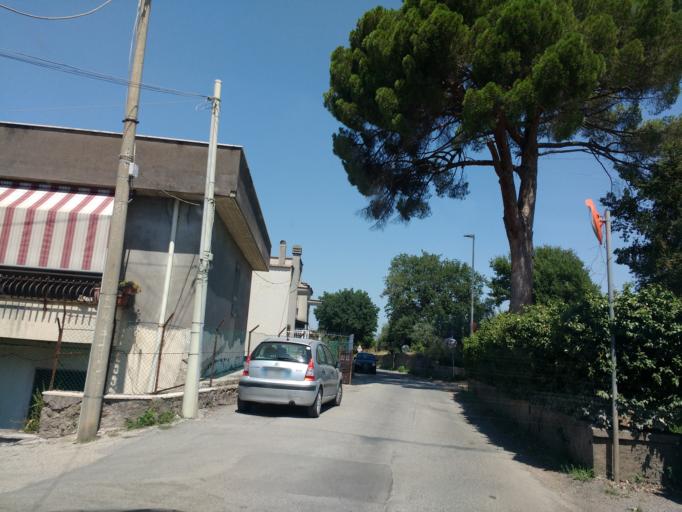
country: IT
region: Latium
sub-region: Citta metropolitana di Roma Capitale
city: Villa Adriana
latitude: 41.9496
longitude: 12.7794
